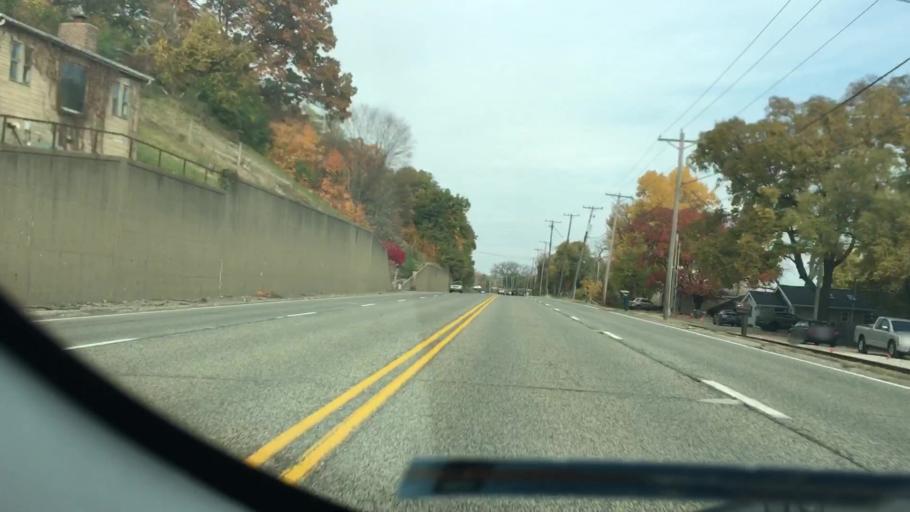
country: US
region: Illinois
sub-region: Peoria County
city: Peoria Heights
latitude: 40.7382
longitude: -89.5528
